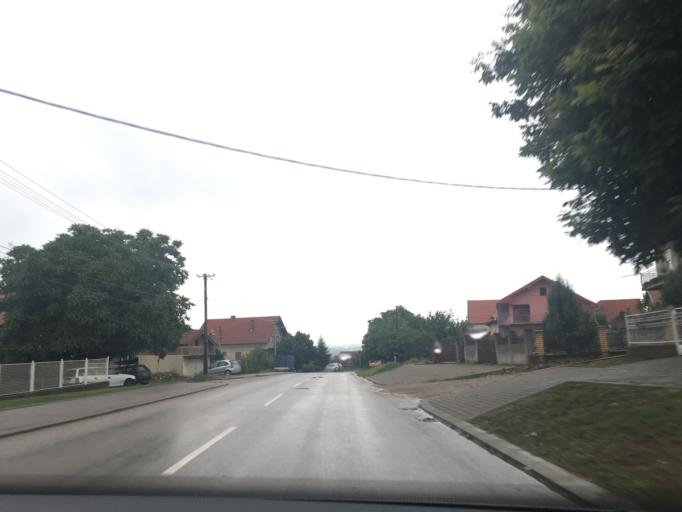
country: RS
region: Central Serbia
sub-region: Nisavski Okrug
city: Aleksinac
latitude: 43.5466
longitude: 21.6943
